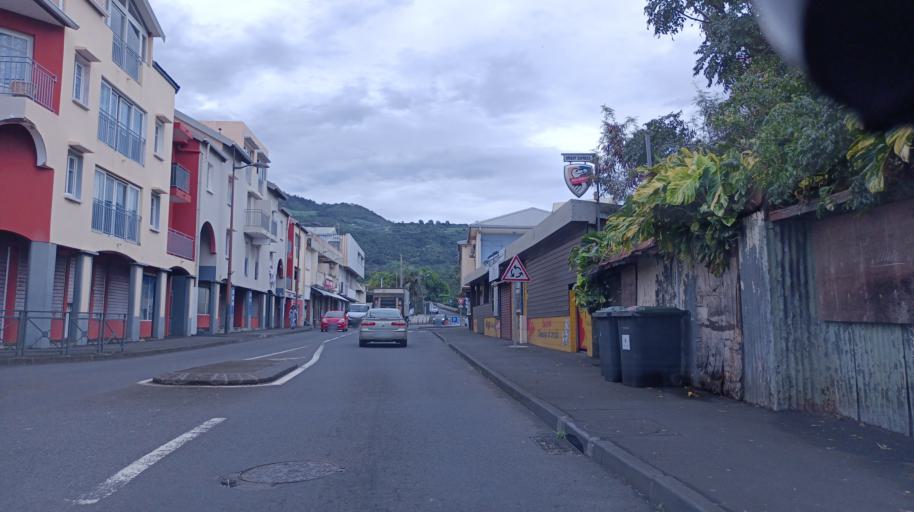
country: RE
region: Reunion
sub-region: Reunion
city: Saint-Joseph
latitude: -21.3774
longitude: 55.6153
